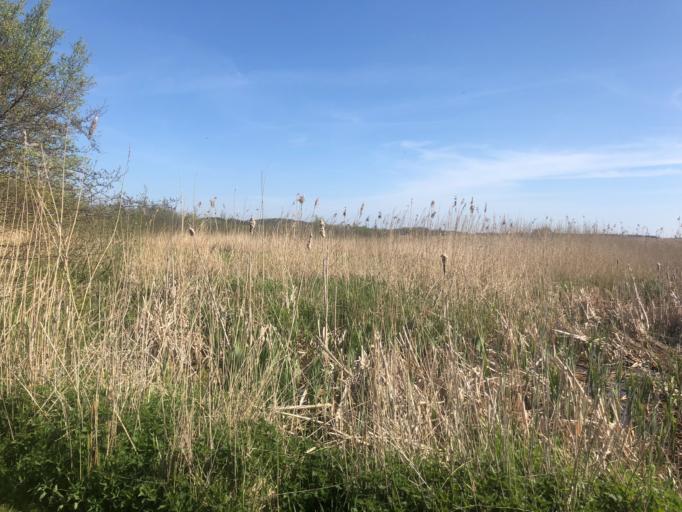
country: DK
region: Central Jutland
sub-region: Holstebro Kommune
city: Vinderup
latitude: 56.5691
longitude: 8.7915
